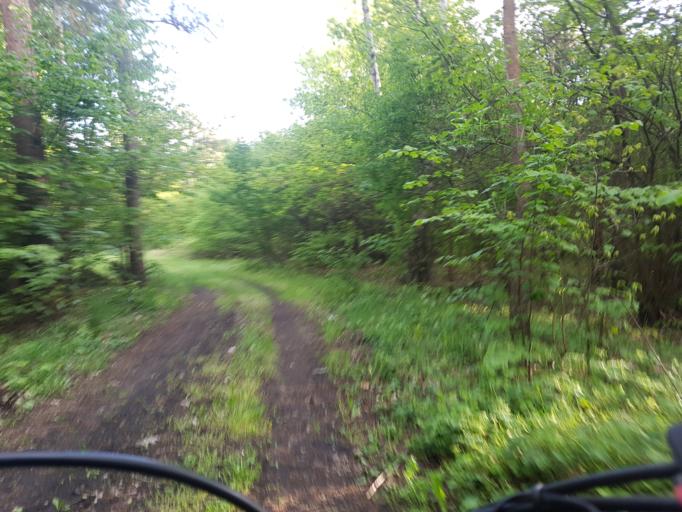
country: DE
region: Brandenburg
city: Trobitz
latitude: 51.5743
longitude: 13.4208
